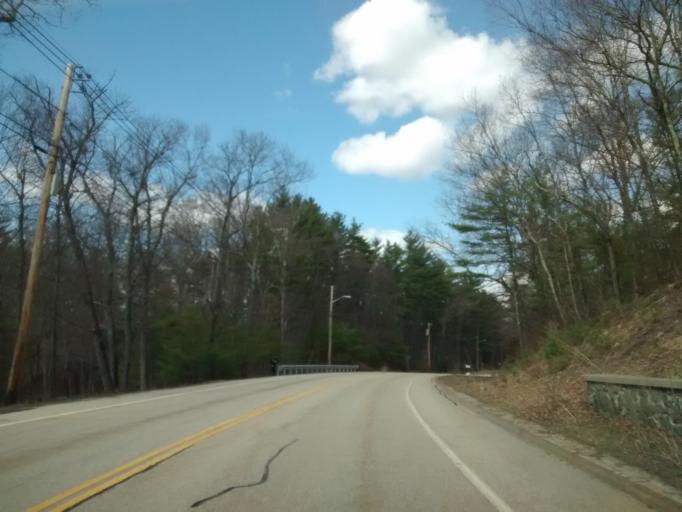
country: US
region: Massachusetts
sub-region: Worcester County
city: Northbridge
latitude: 42.1538
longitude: -71.6263
